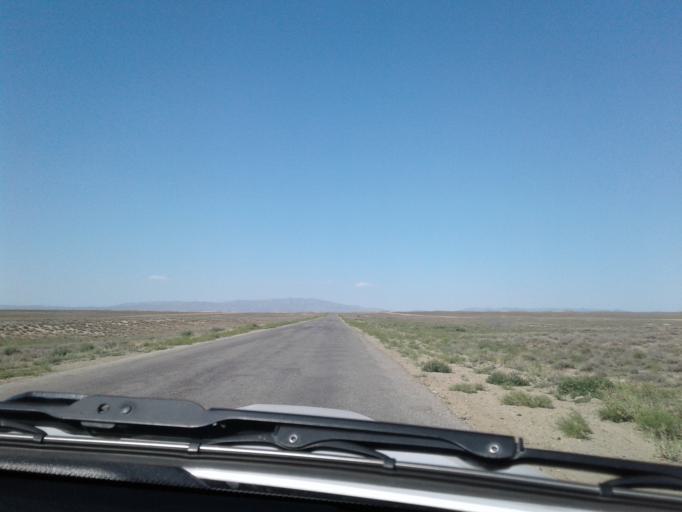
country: TM
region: Balkan
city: Magtymguly
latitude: 38.6111
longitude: 56.2148
